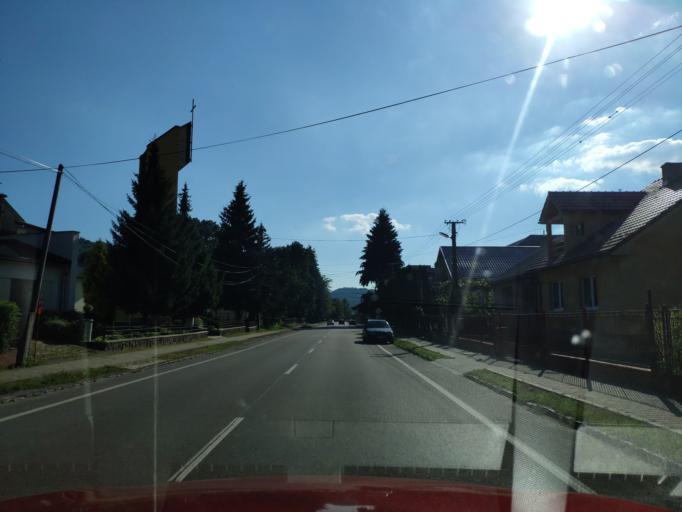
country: SK
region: Presovsky
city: Snina
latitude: 49.0025
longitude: 22.2311
